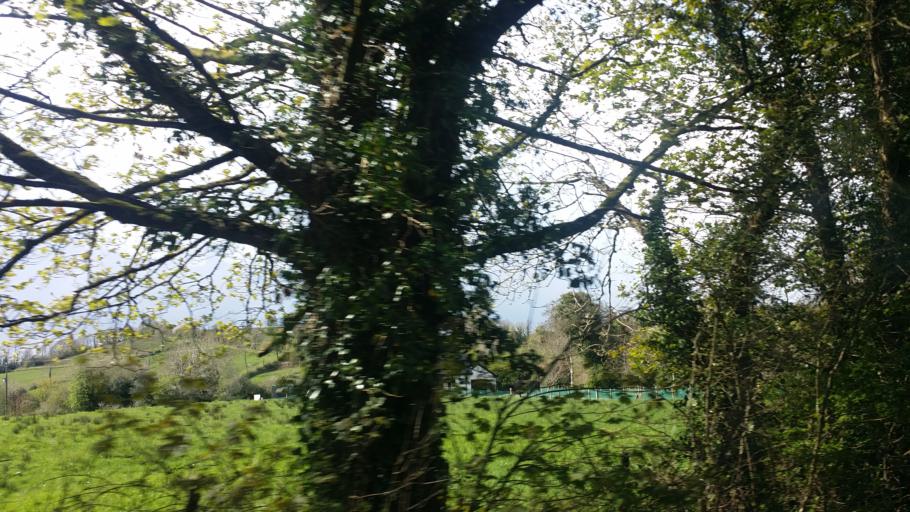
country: GB
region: Northern Ireland
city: Irvinestown
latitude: 54.4402
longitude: -7.7939
